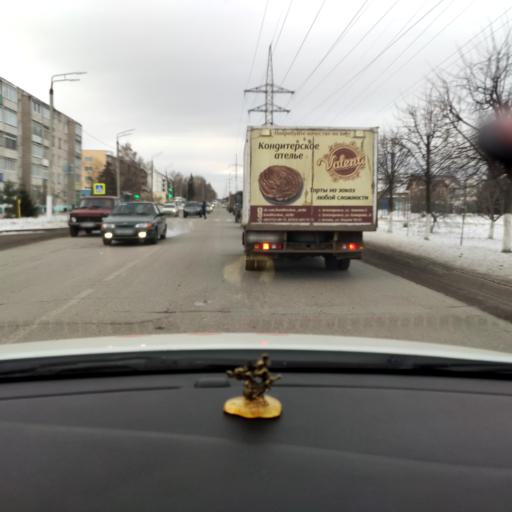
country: RU
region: Tatarstan
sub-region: Zelenodol'skiy Rayon
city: Zelenodolsk
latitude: 55.8516
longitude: 48.5272
